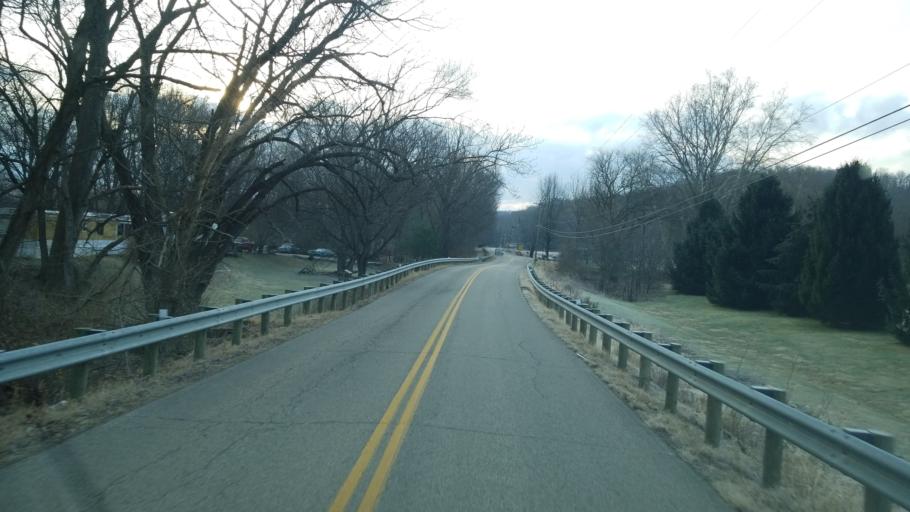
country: US
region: Ohio
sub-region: Ross County
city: Chillicothe
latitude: 39.2625
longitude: -82.9170
